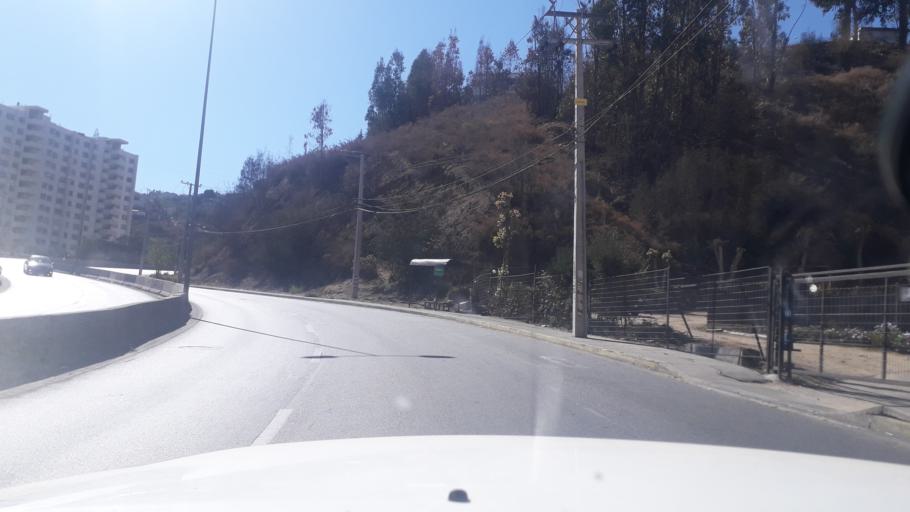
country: CL
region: Valparaiso
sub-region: Provincia de Valparaiso
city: Vina del Mar
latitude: -33.0366
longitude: -71.5162
